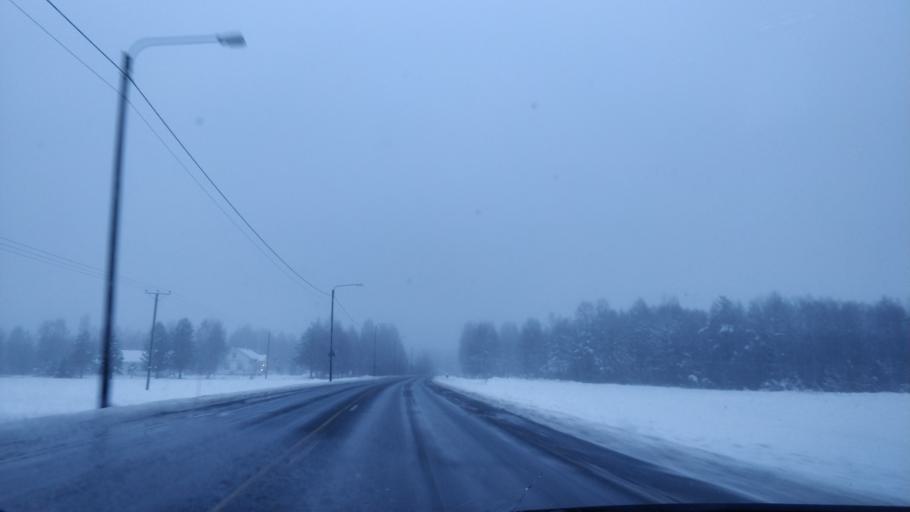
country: FI
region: Lapland
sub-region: Kemi-Tornio
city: Tervola
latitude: 66.1525
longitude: 24.9944
